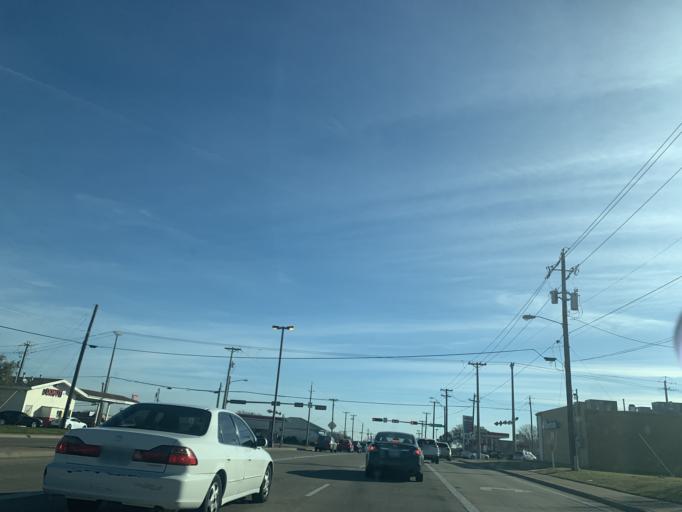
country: US
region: Texas
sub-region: Dallas County
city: DeSoto
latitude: 32.5897
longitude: -96.8580
